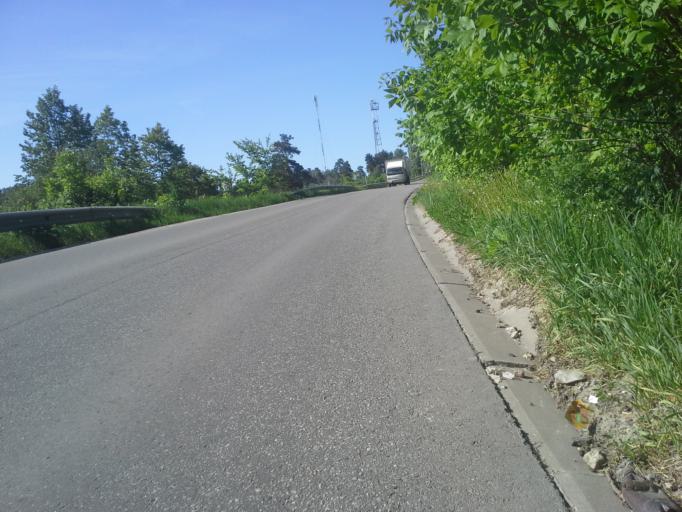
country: RU
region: Moskovskaya
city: Vatutinki
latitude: 55.4490
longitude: 37.3988
